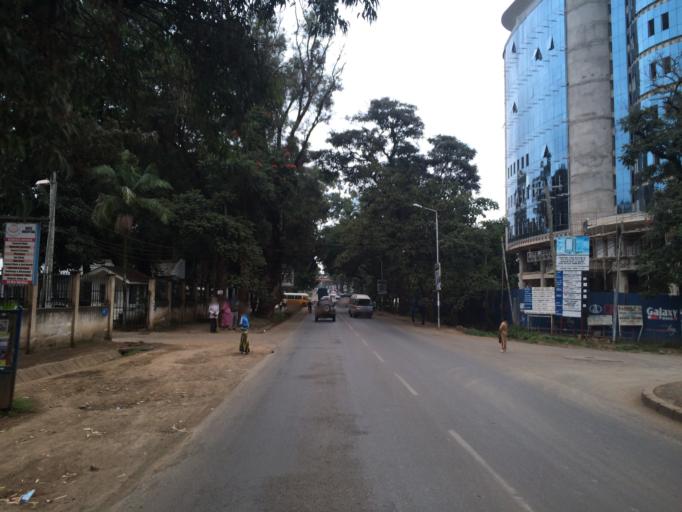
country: TZ
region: Arusha
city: Arusha
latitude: -3.3750
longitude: 36.6988
